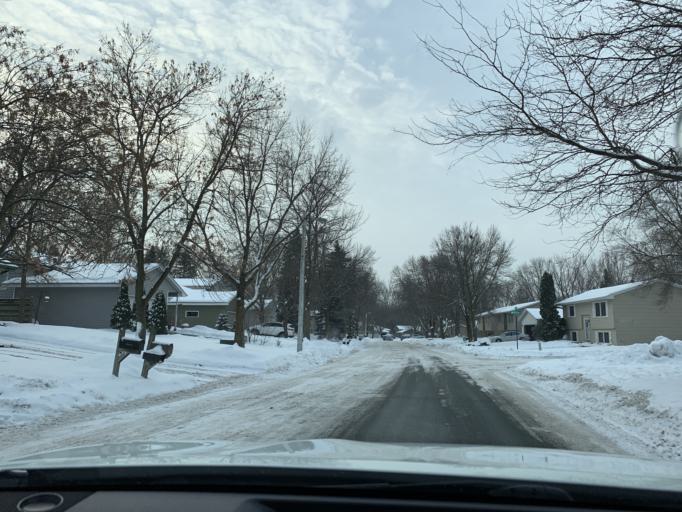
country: US
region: Minnesota
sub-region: Anoka County
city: Coon Rapids
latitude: 45.1606
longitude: -93.2876
